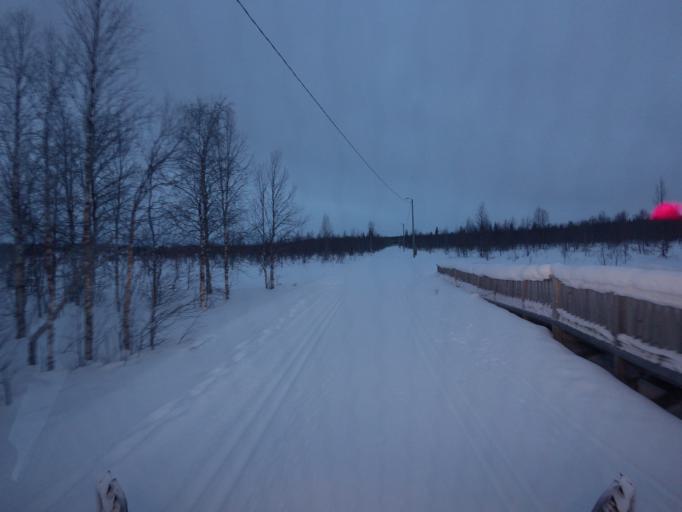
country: FI
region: Lapland
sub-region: Tunturi-Lappi
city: Kolari
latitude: 67.6136
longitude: 24.1673
